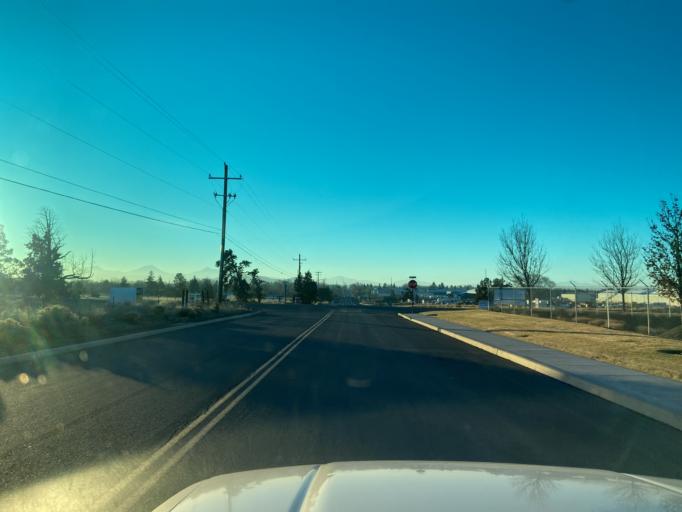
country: US
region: Oregon
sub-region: Deschutes County
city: Redmond
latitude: 44.2766
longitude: -121.1581
